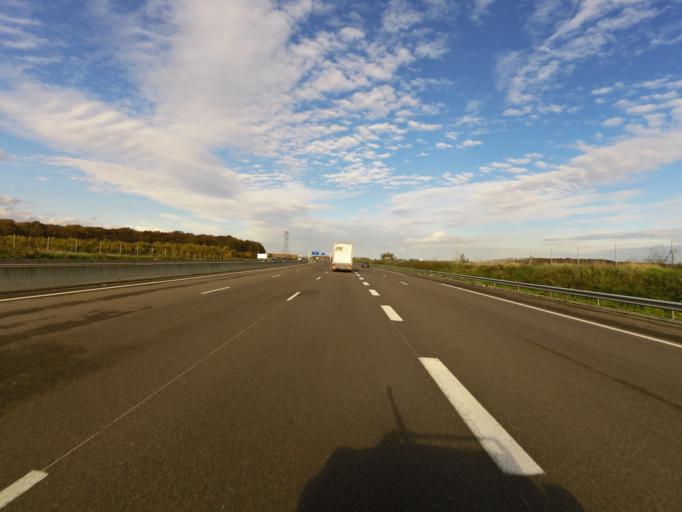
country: FR
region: Bourgogne
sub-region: Departement de la Cote-d'Or
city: Perrigny-les-Dijon
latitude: 47.2338
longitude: 5.0212
